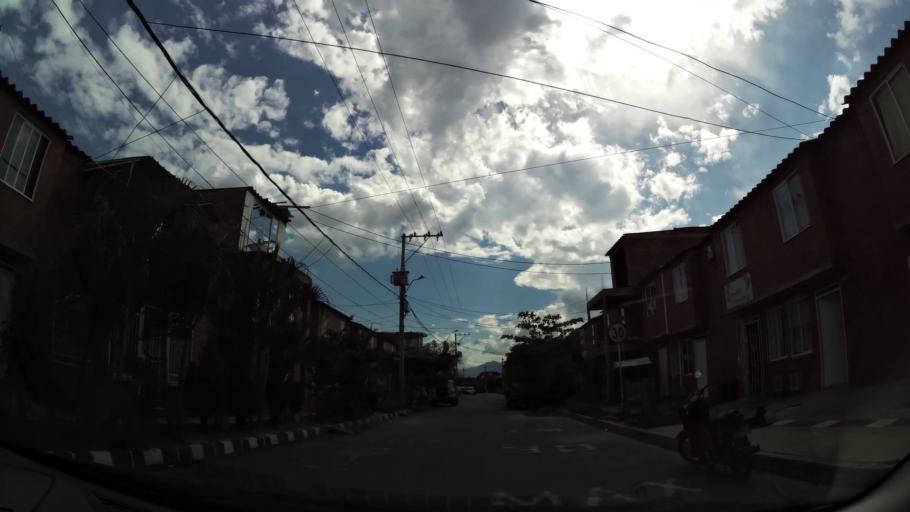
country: CO
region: Valle del Cauca
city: Cali
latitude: 3.3929
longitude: -76.5083
